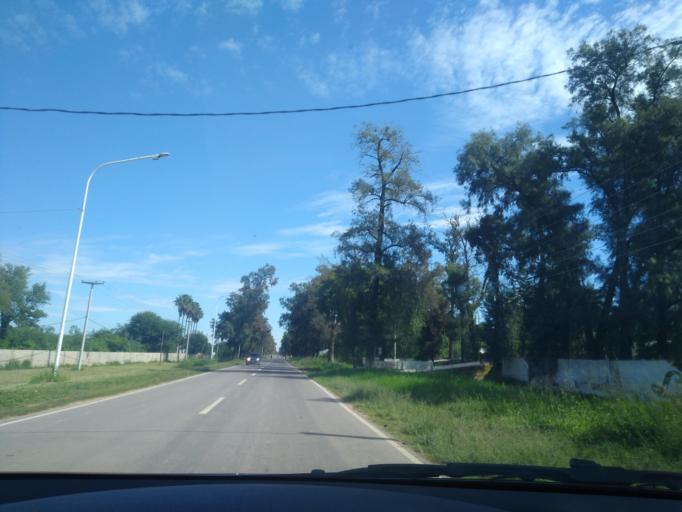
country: AR
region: Chaco
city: Presidencia Roque Saenz Pena
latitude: -26.7772
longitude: -60.4061
